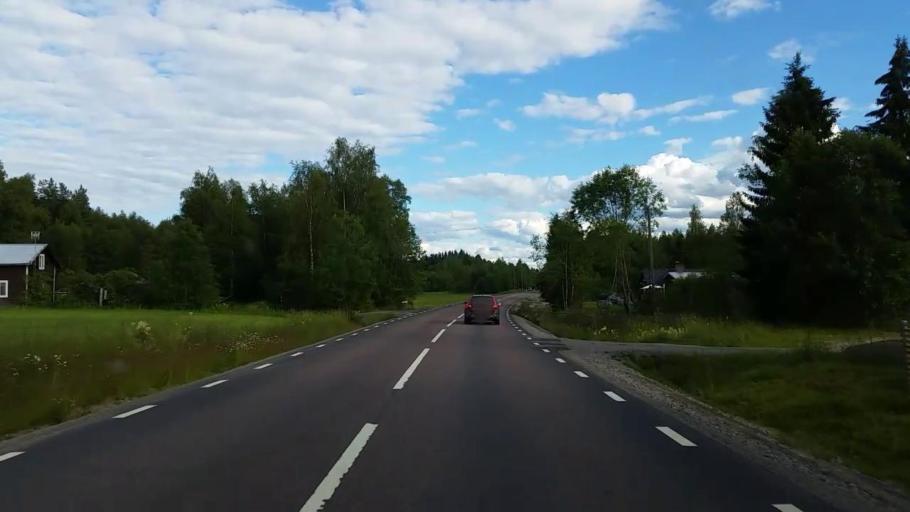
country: SE
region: Gaevleborg
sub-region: Ljusdals Kommun
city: Ljusdal
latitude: 61.8605
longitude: 15.9853
